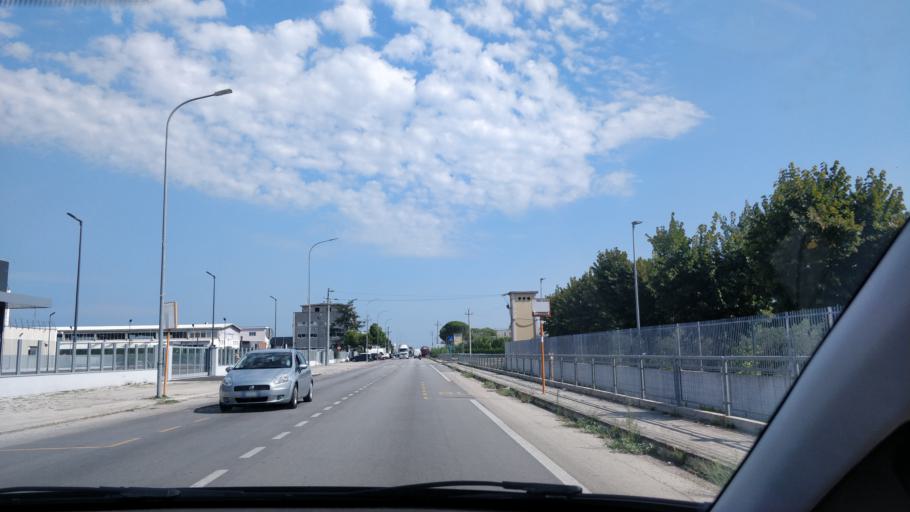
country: IT
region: Abruzzo
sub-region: Provincia di Pescara
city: Santa Teresa
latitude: 42.4092
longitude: 14.1657
